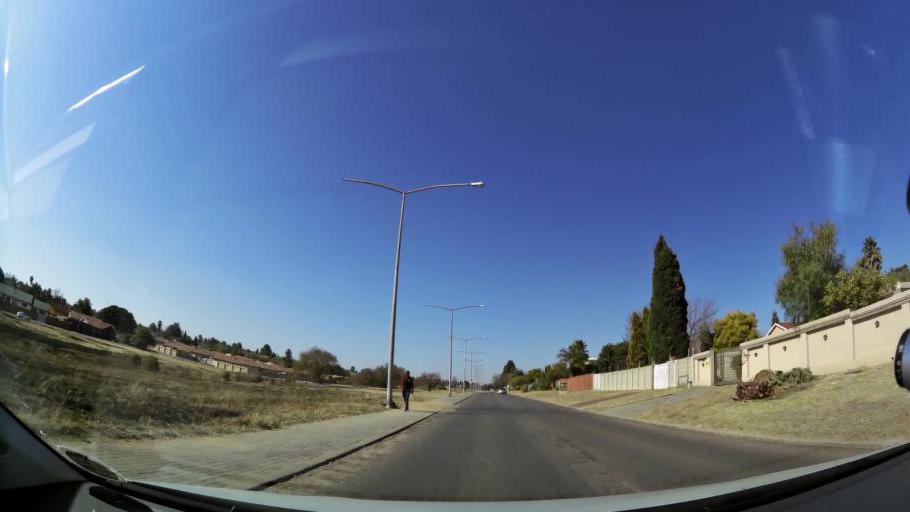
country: ZA
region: Gauteng
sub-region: Ekurhuleni Metropolitan Municipality
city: Tembisa
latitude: -26.0392
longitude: 28.2256
